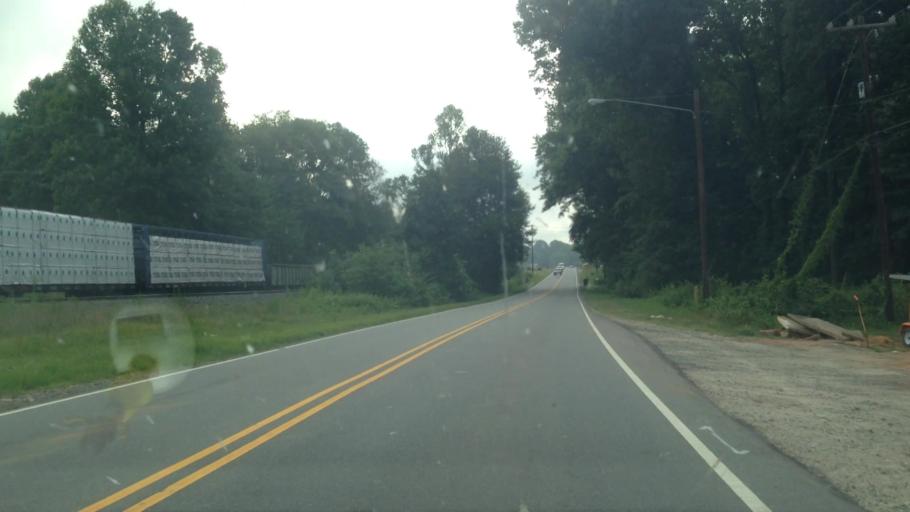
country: US
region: North Carolina
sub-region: Forsyth County
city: Kernersville
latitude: 36.1369
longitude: -80.1041
